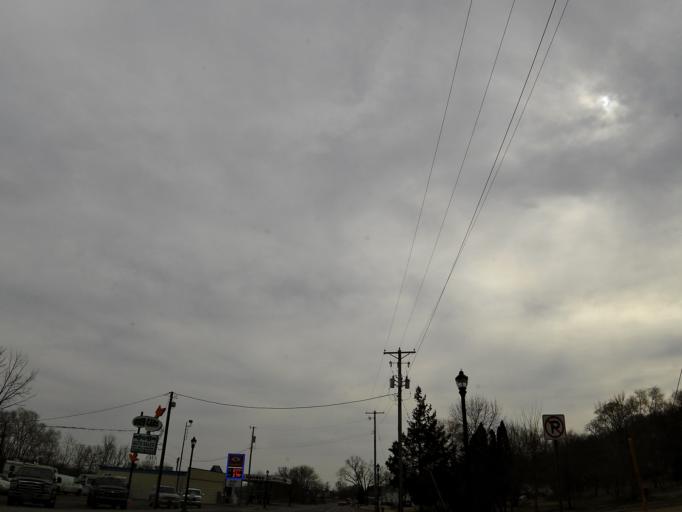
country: US
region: Minnesota
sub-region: Washington County
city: Newport
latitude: 44.8587
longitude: -93.0210
